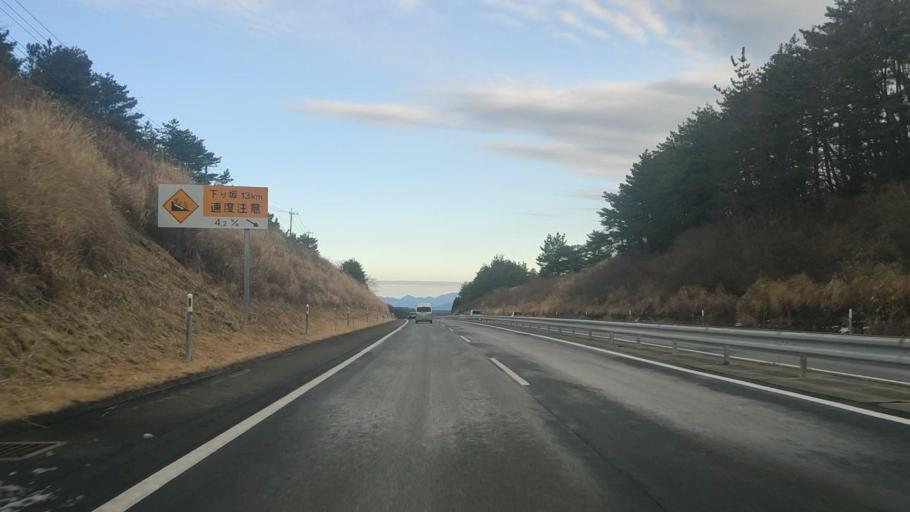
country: JP
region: Oita
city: Beppu
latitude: 33.3216
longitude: 131.4136
